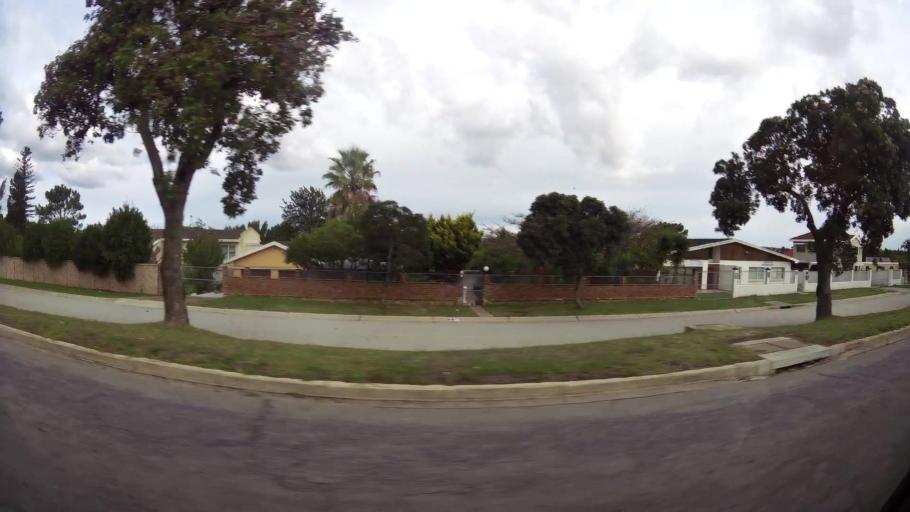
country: ZA
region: Eastern Cape
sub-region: Nelson Mandela Bay Metropolitan Municipality
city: Port Elizabeth
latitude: -33.9464
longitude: 25.5480
